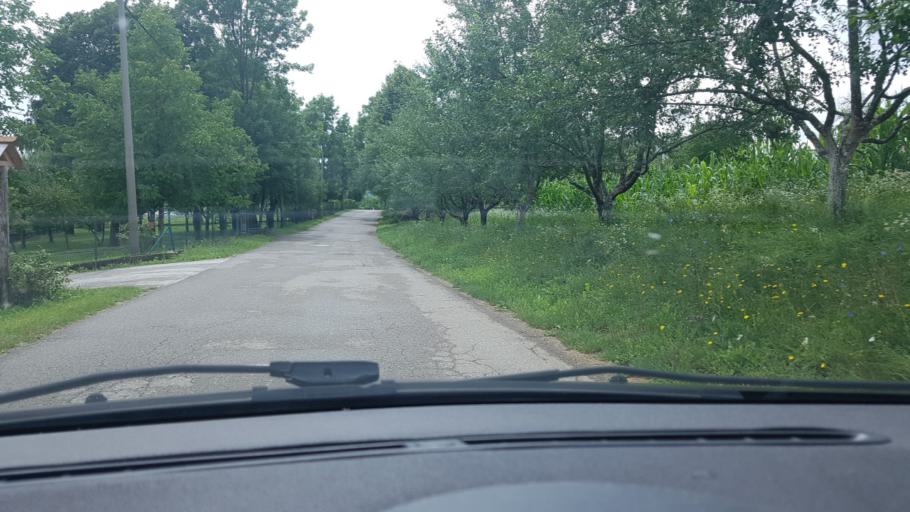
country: HR
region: Licko-Senjska
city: Jezerce
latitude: 44.9541
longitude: 15.6735
